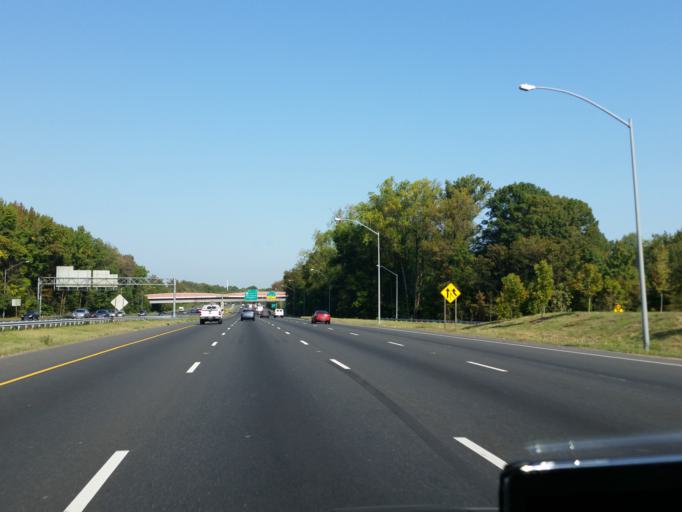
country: US
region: Maryland
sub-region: Prince George's County
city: Largo
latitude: 38.8936
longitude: -76.8475
